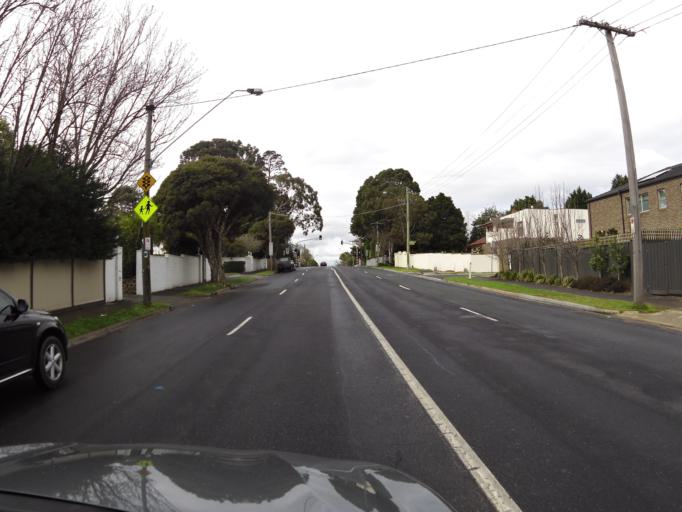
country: AU
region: Victoria
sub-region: Boroondara
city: Hawthorn East
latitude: -37.8164
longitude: 145.0509
